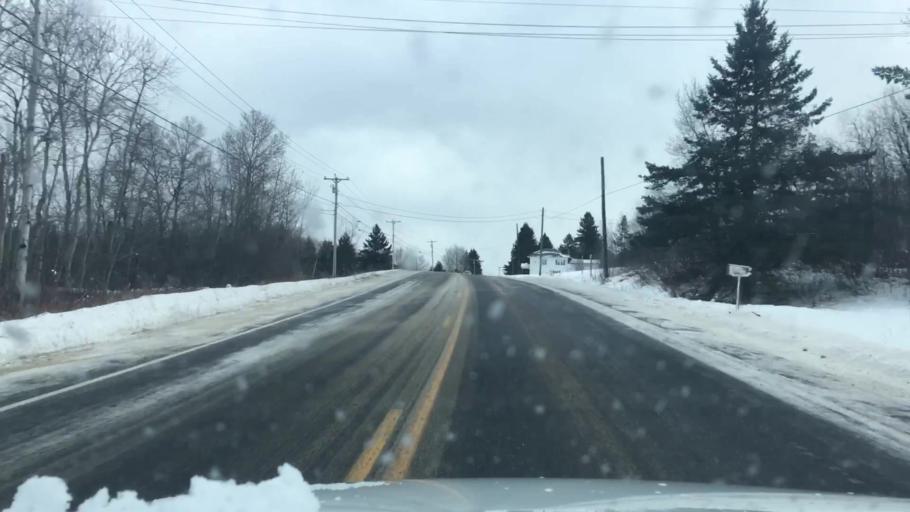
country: US
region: Maine
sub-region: Aroostook County
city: Madawaska
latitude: 47.3189
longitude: -68.1670
